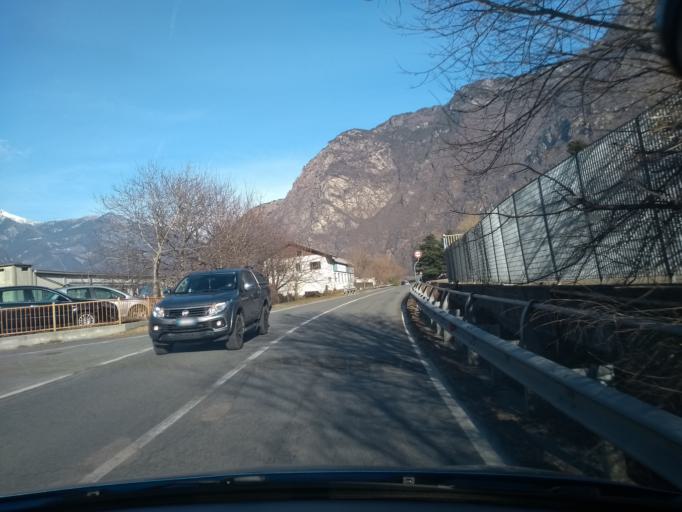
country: IT
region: Aosta Valley
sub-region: Valle d'Aosta
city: Arnad
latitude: 45.6374
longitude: 7.7198
